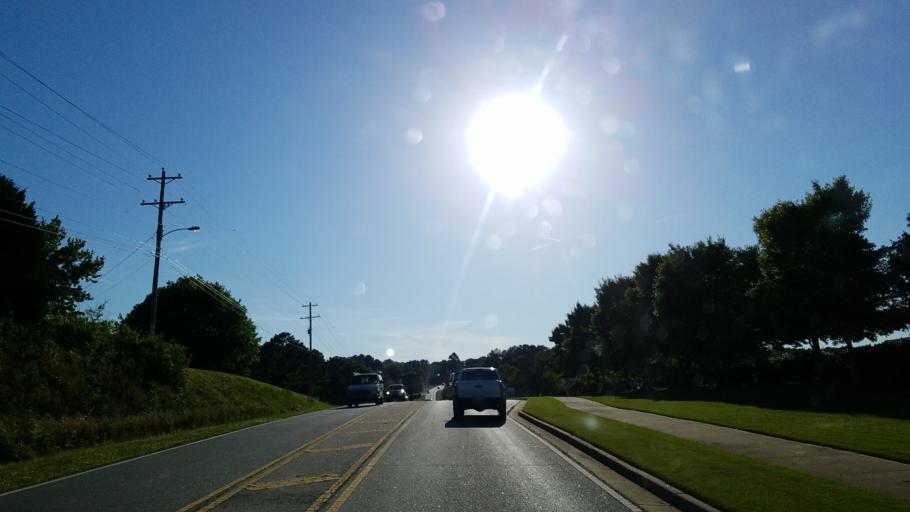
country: US
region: Georgia
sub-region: Cherokee County
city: Holly Springs
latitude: 34.1680
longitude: -84.4520
